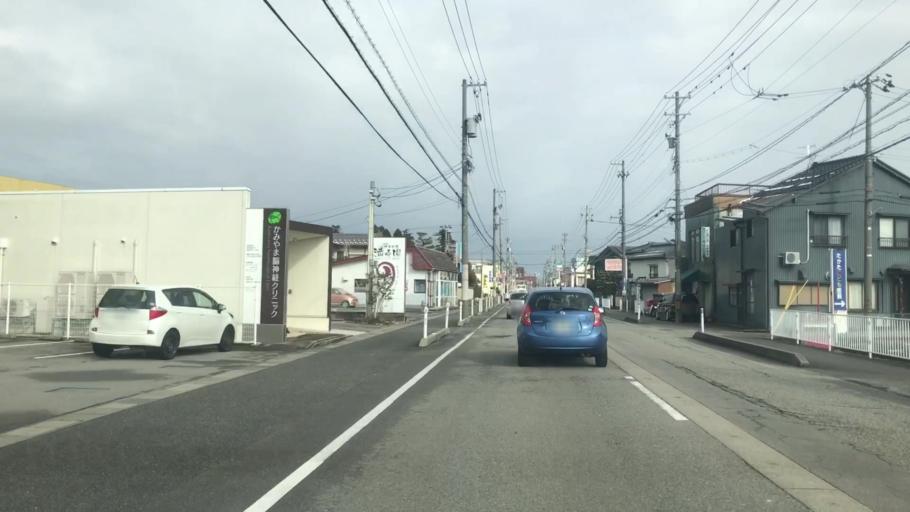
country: JP
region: Toyama
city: Toyama-shi
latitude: 36.6579
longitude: 137.2189
